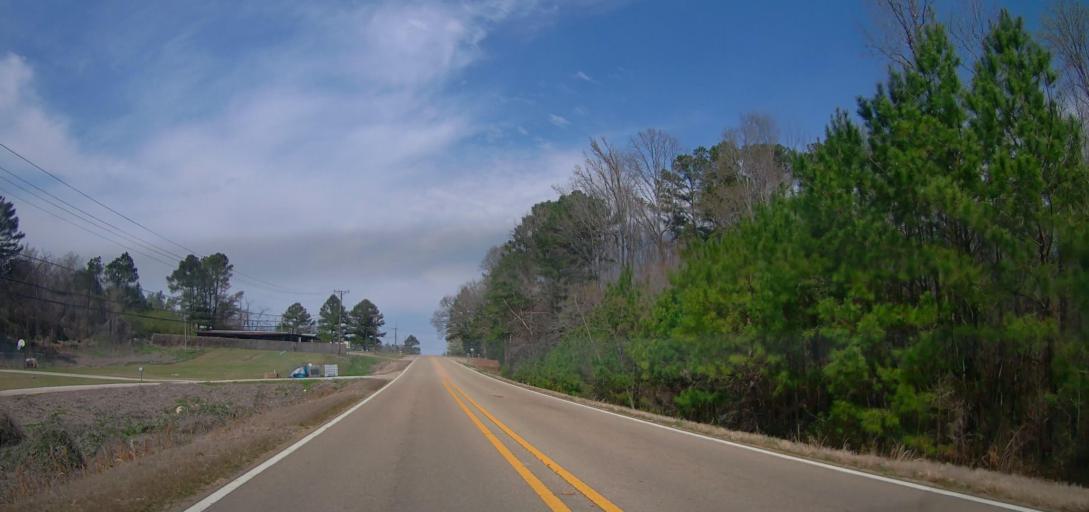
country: US
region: Mississippi
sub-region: Union County
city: New Albany
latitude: 34.4510
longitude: -88.9711
